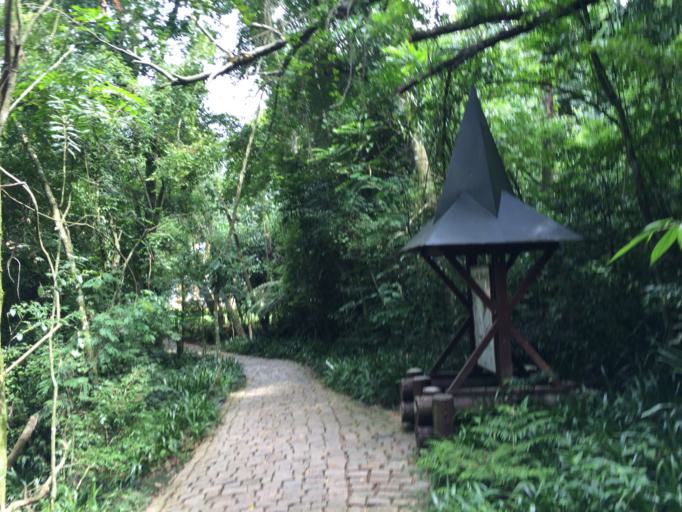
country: BR
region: Parana
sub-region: Curitiba
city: Curitiba
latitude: -25.4063
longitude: -49.2857
